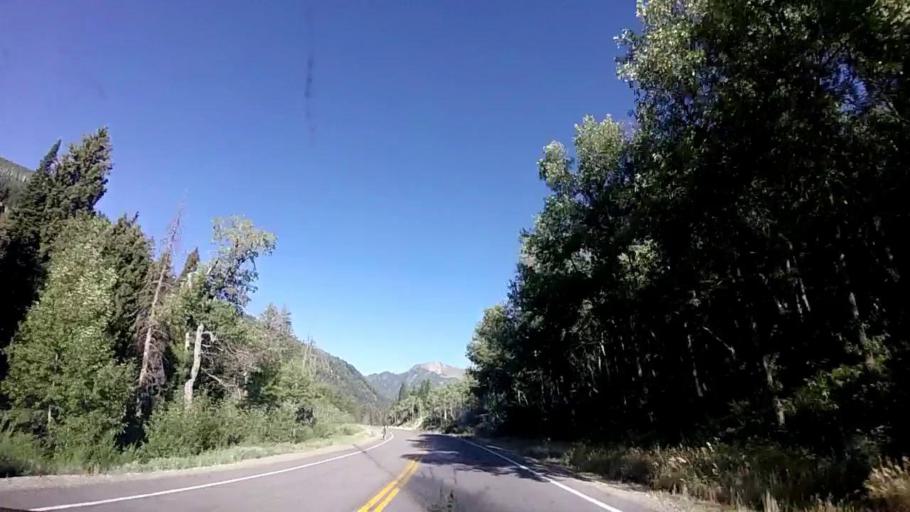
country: US
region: Utah
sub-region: Summit County
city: Snyderville
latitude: 40.6386
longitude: -111.6229
